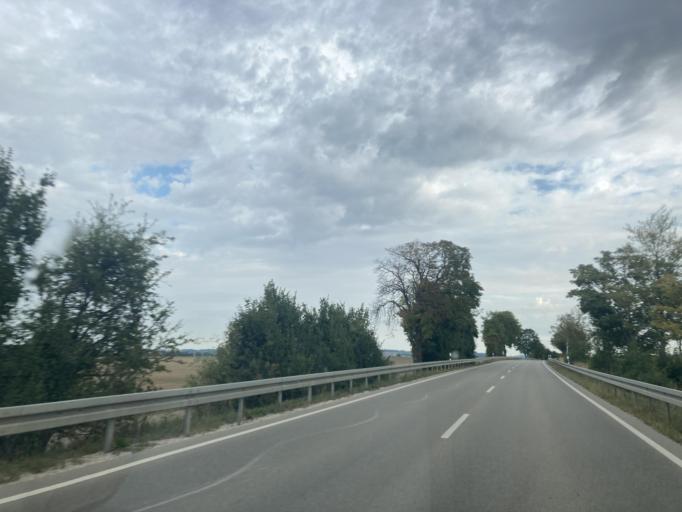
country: DE
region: Bavaria
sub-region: Swabia
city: Munningen
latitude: 48.9150
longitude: 10.5686
